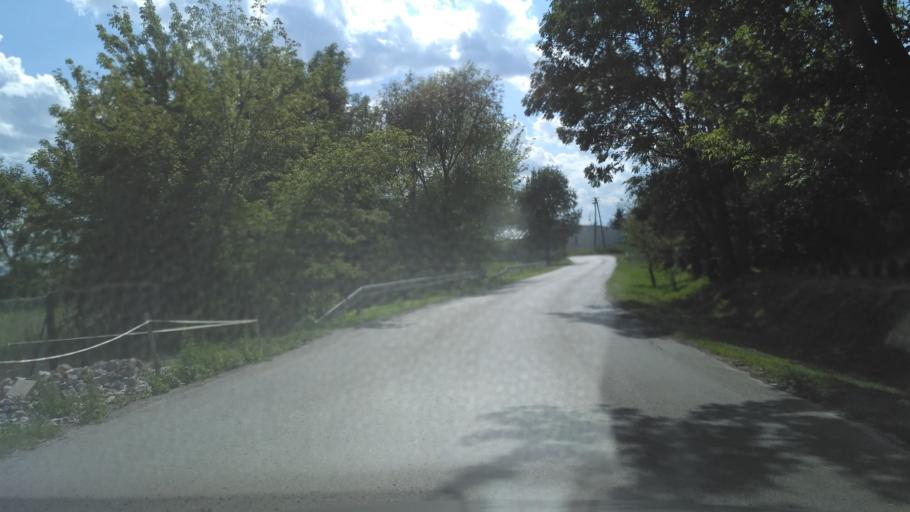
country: PL
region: Lublin Voivodeship
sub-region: Powiat leczynski
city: Milejow
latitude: 51.2141
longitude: 22.8888
